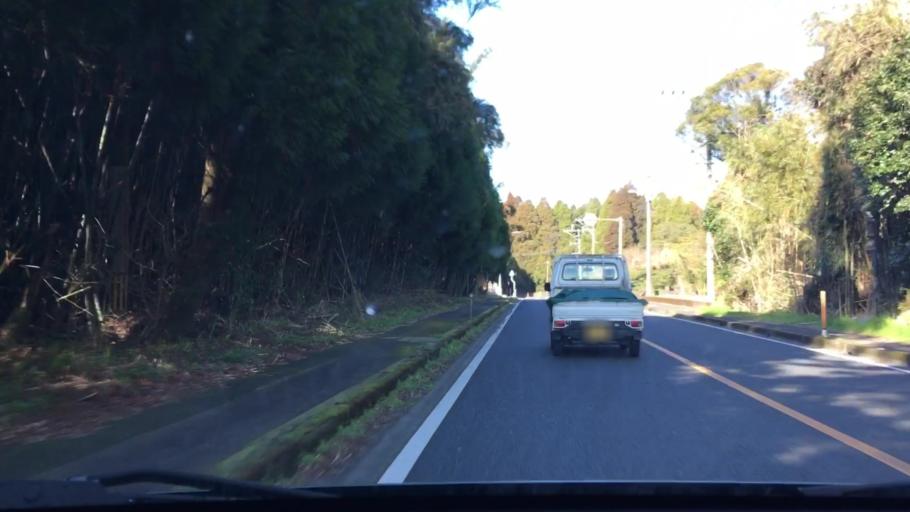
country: JP
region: Kagoshima
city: Kokubu-matsuki
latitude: 31.6718
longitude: 130.8628
